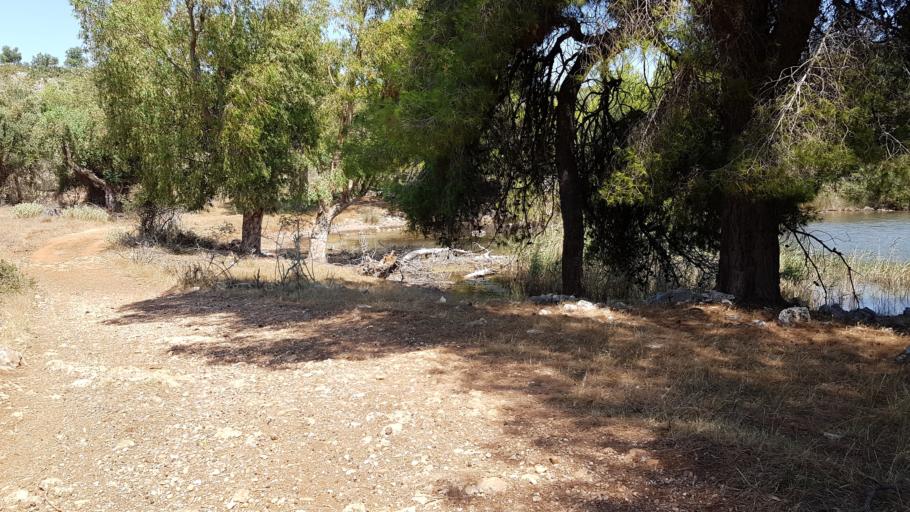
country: AL
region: Vlore
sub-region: Rrethi i Sarandes
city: Xarre
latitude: 39.7556
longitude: 19.9949
